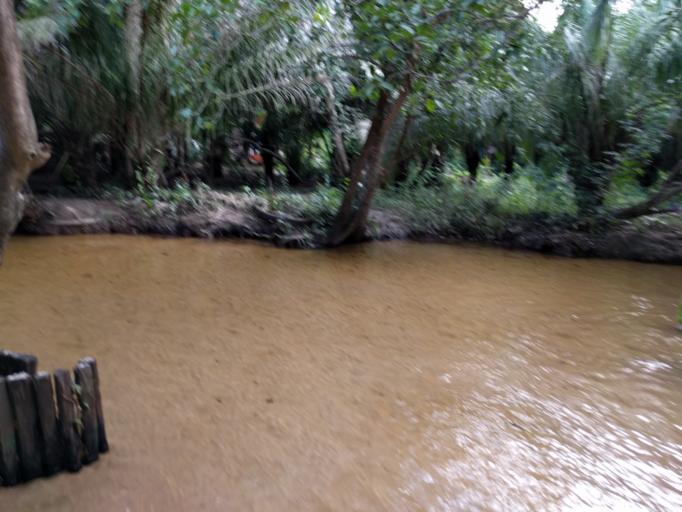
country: BO
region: Santa Cruz
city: Robore
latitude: -18.4495
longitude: -59.5143
